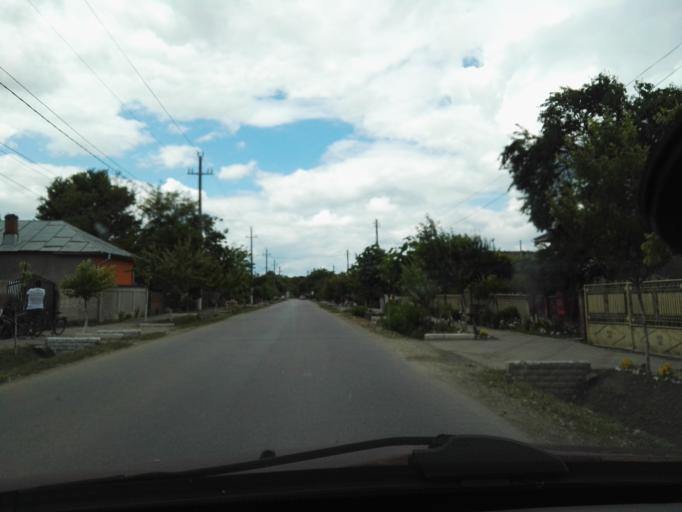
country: RO
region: Giurgiu
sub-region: Comuna Comana
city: Gradistea
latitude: 44.2096
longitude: 26.1514
